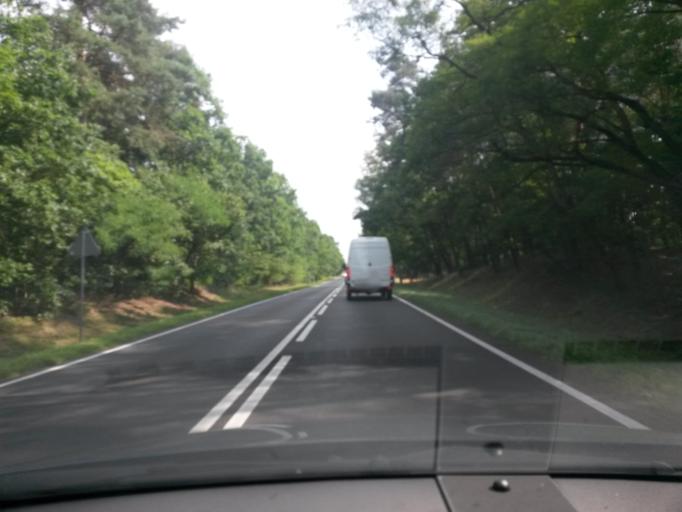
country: PL
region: Greater Poland Voivodeship
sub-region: Powiat sremski
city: Srem
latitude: 52.1517
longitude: 17.0352
